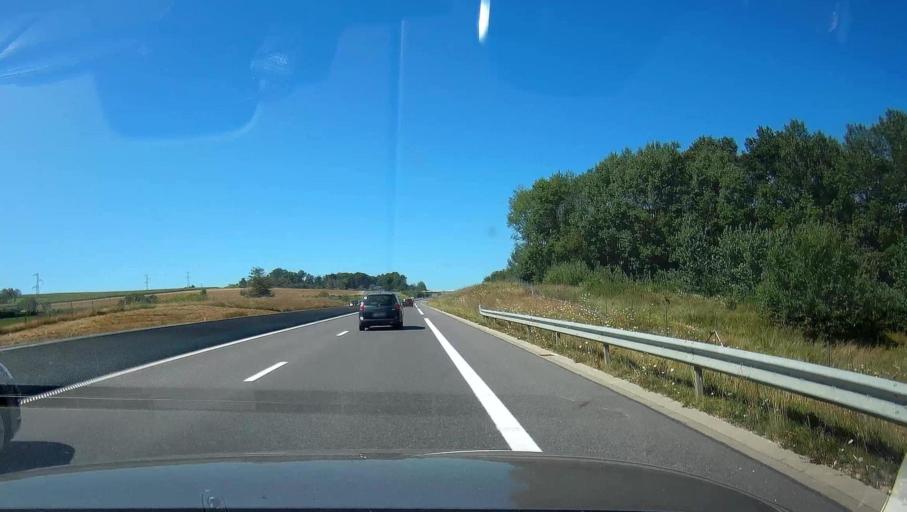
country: FR
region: Champagne-Ardenne
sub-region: Departement des Ardennes
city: Prix-les-Mezieres
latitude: 49.7367
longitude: 4.6842
